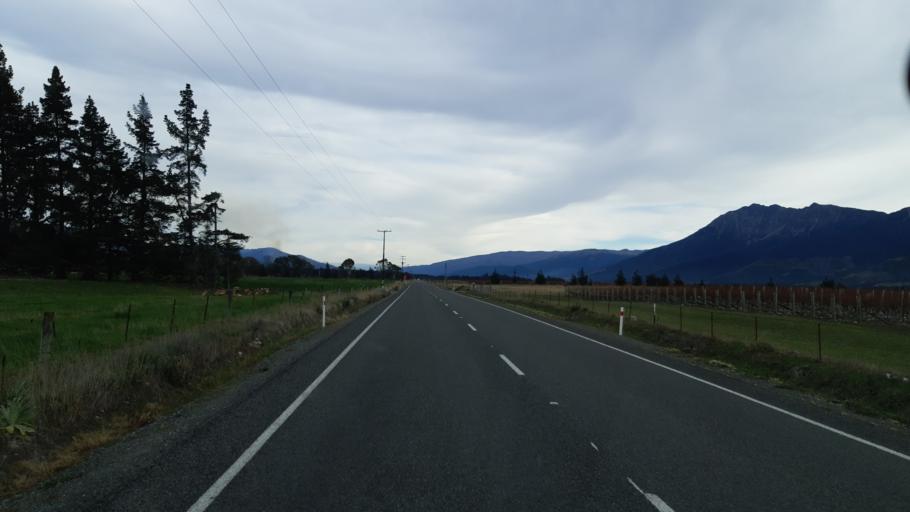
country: NZ
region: Tasman
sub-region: Tasman District
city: Richmond
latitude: -41.6192
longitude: 173.3694
